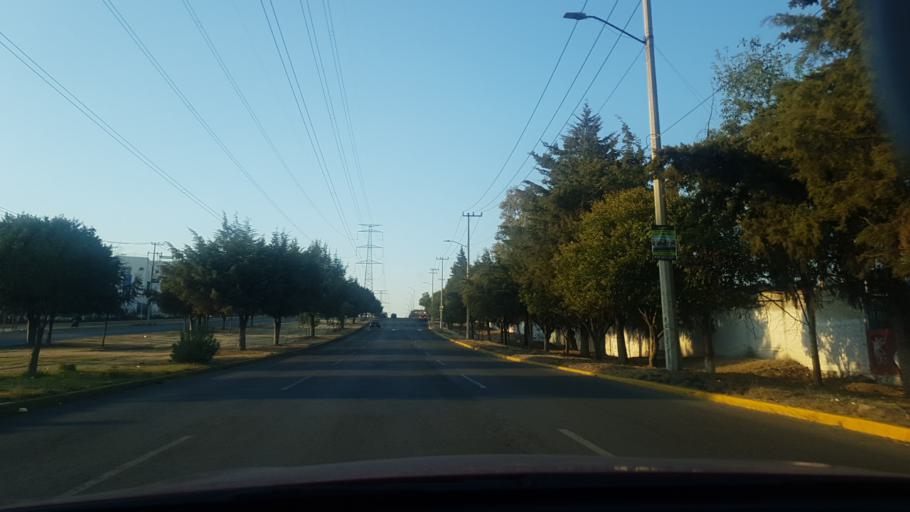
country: MX
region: Mexico
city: Cuautitlan Izcalli
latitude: 19.6371
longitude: -99.2205
